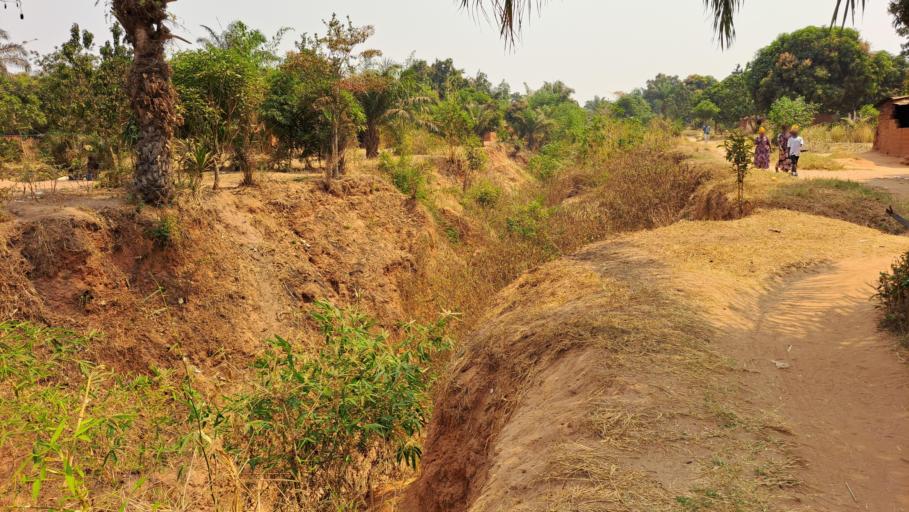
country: CD
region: Kasai-Oriental
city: Mbuji-Mayi
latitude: -6.0984
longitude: 23.5622
